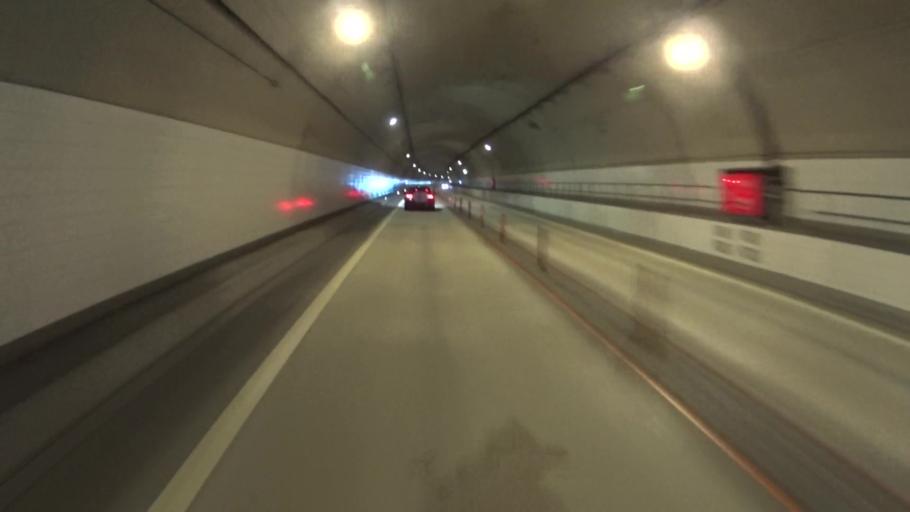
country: JP
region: Kyoto
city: Miyazu
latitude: 35.5333
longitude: 135.1669
